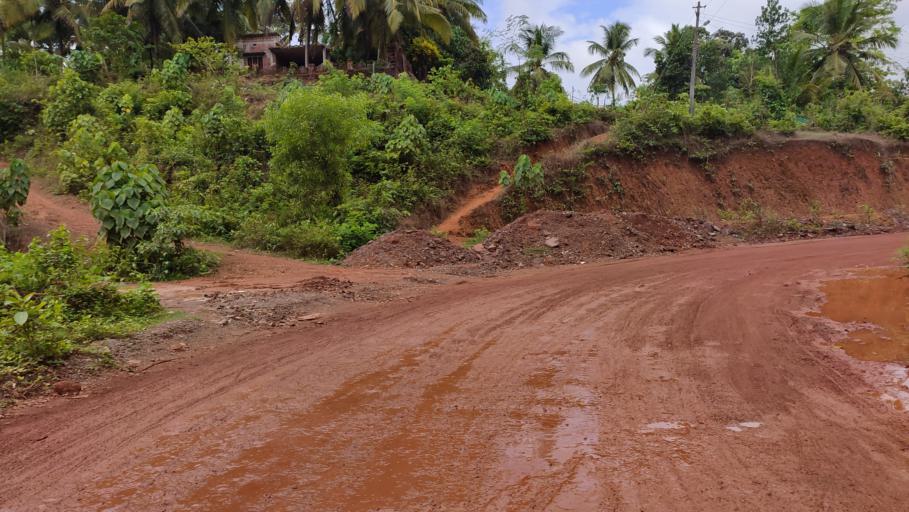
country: IN
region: Kerala
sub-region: Kasaragod District
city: Kasaragod
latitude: 12.5290
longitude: 75.0716
